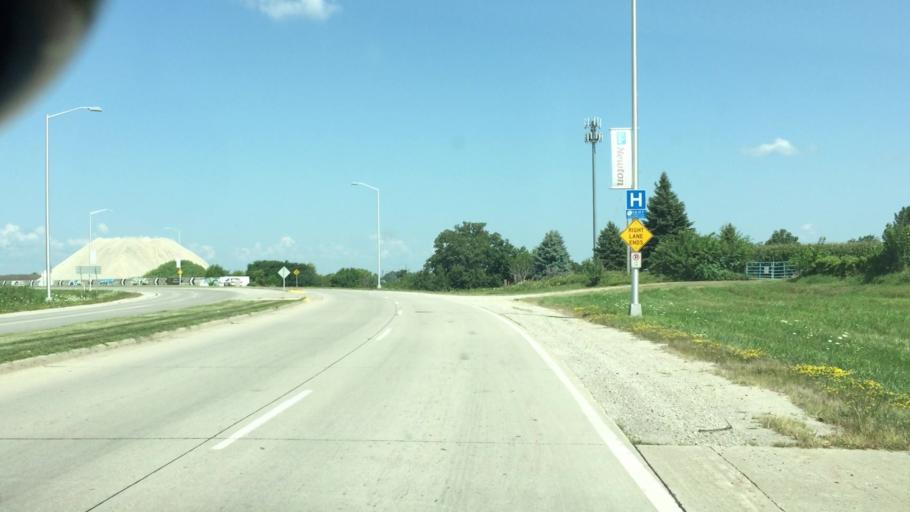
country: US
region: Iowa
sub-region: Jasper County
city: Newton
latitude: 41.6851
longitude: -92.9999
